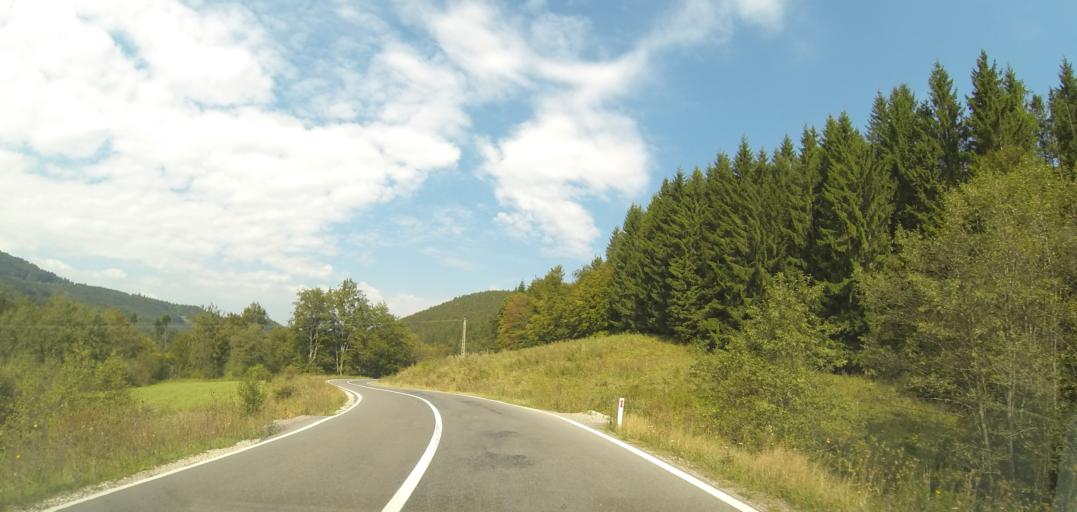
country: RO
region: Brasov
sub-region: Comuna Tarlungeni
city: Zizin
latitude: 45.5402
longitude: 25.8338
